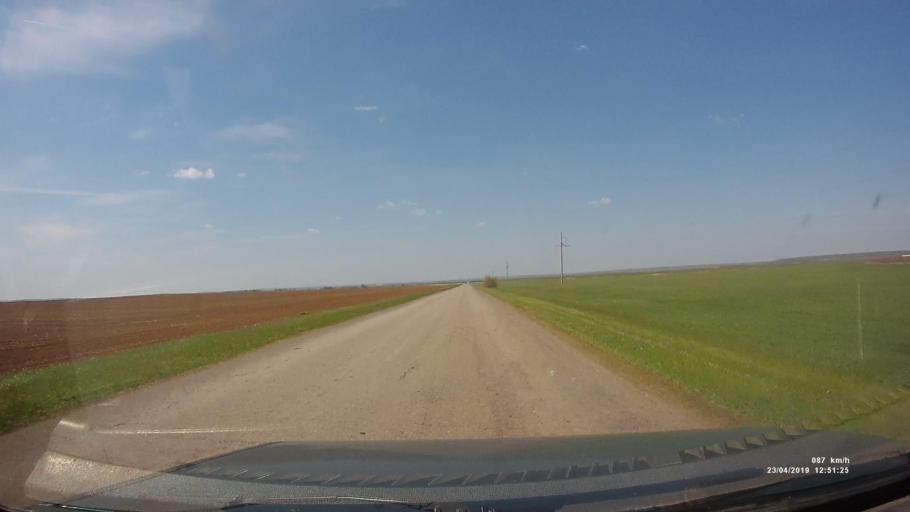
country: RU
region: Kalmykiya
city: Yashalta
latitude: 46.5547
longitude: 42.6231
